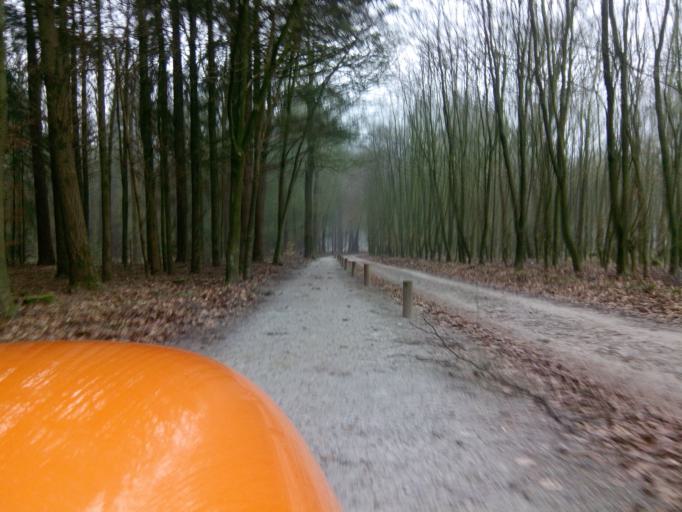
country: NL
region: Gelderland
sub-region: Gemeente Barneveld
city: Stroe
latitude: 52.2160
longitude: 5.6717
